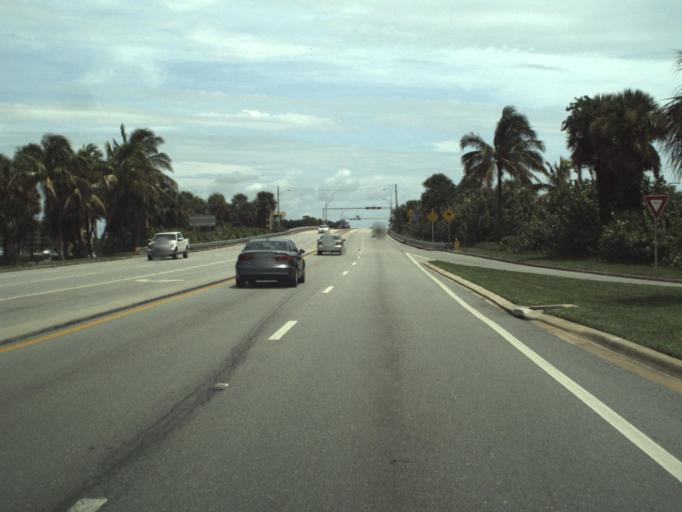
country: US
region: Florida
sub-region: Palm Beach County
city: Jupiter
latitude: 26.9444
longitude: -80.0845
